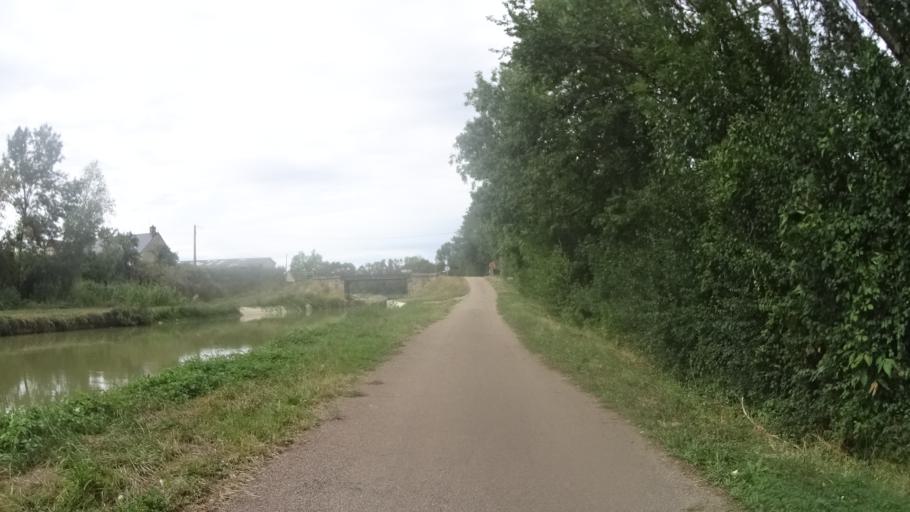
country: FR
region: Bourgogne
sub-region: Departement de la Nievre
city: Sermoise-sur-Loire
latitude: 46.9585
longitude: 3.1982
